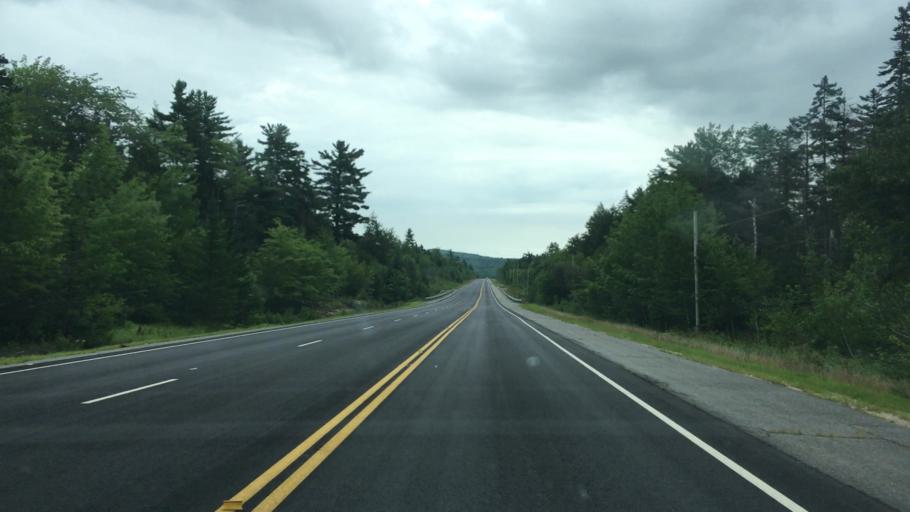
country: US
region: Maine
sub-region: Washington County
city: Cherryfield
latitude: 44.8748
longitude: -67.8984
